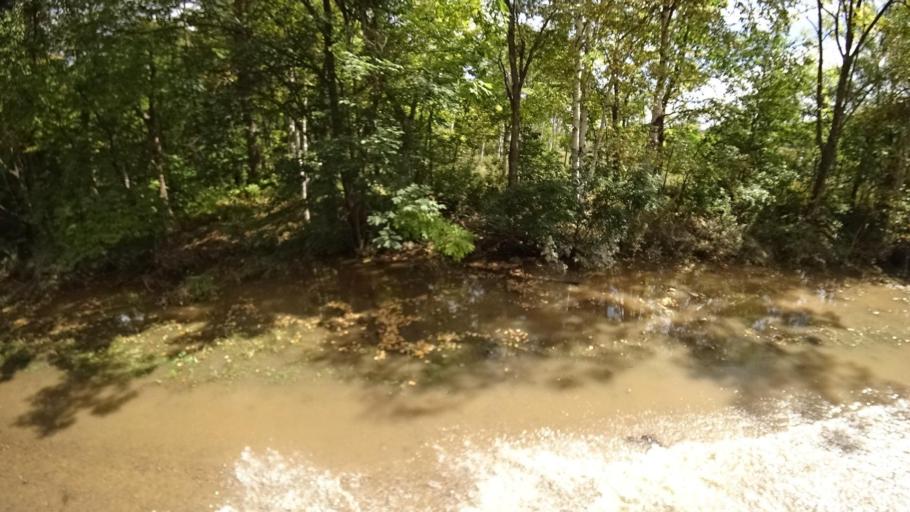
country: RU
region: Primorskiy
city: Yakovlevka
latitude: 44.6630
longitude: 133.7505
